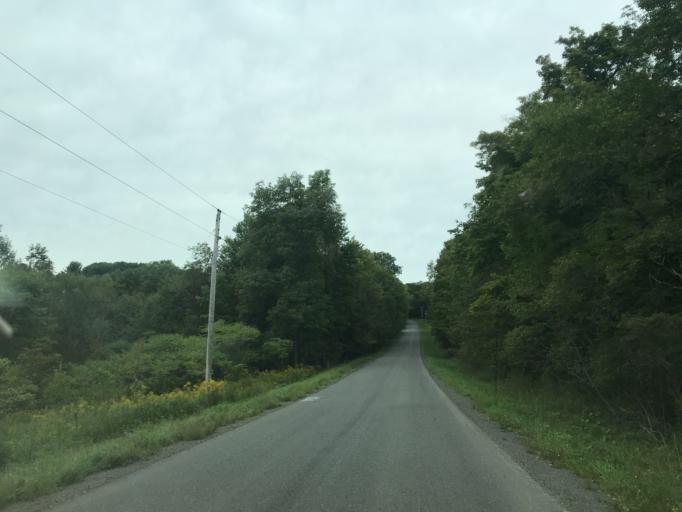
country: US
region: New York
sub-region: Otsego County
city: Worcester
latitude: 42.5244
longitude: -74.6628
